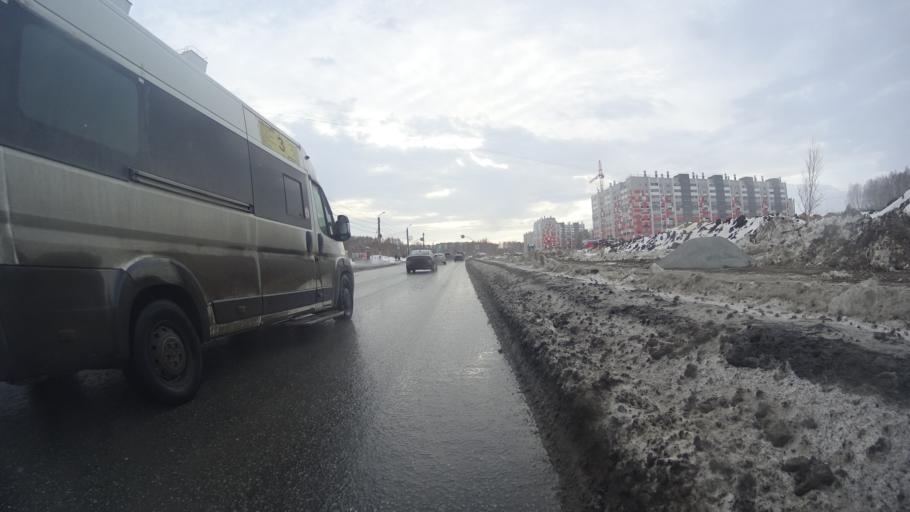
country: RU
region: Chelyabinsk
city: Roshchino
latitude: 55.2186
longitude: 61.2929
